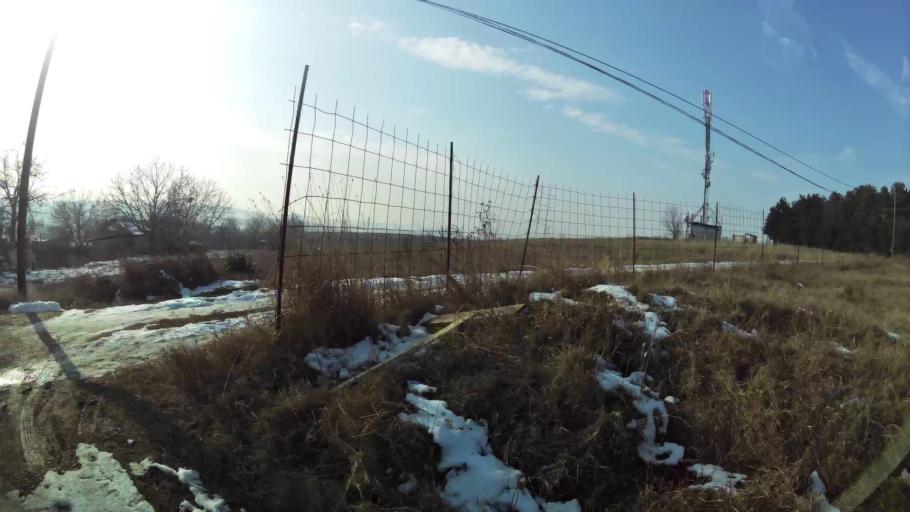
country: MK
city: Creshevo
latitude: 42.0140
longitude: 21.5031
